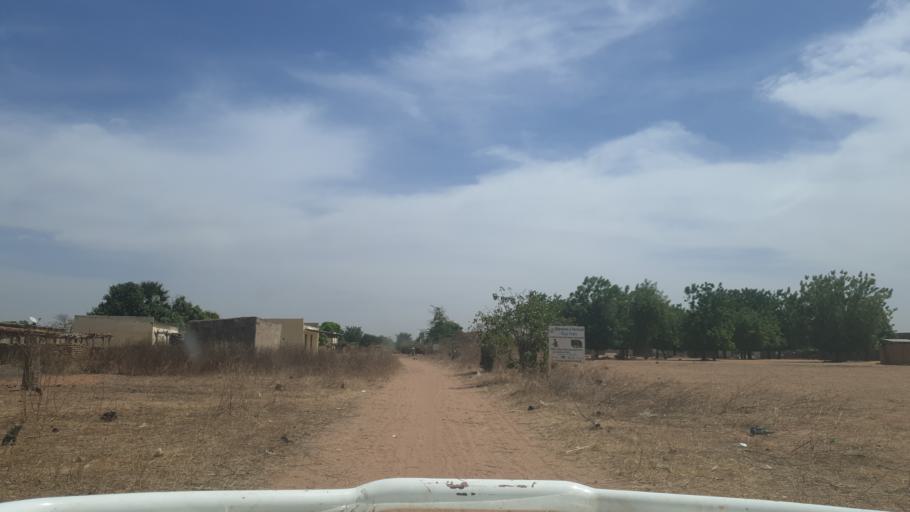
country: ML
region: Sikasso
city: Yorosso
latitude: 12.2911
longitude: -4.6552
